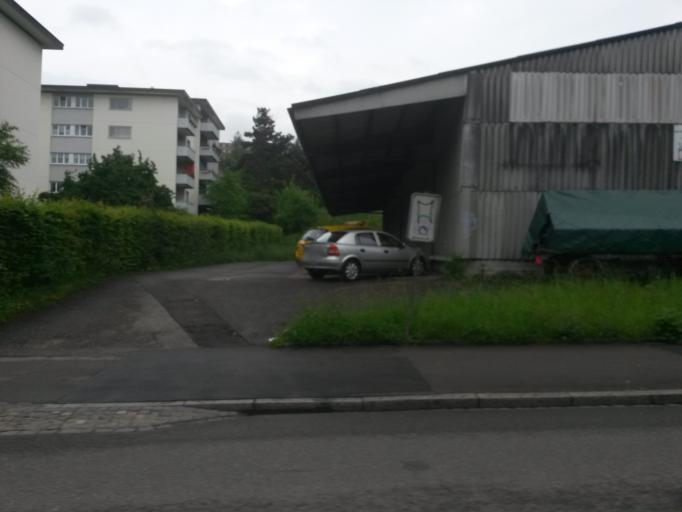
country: CH
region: Zurich
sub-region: Bezirk Zuerich
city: Zuerich (Kreis 11)
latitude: 47.4142
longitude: 8.5219
